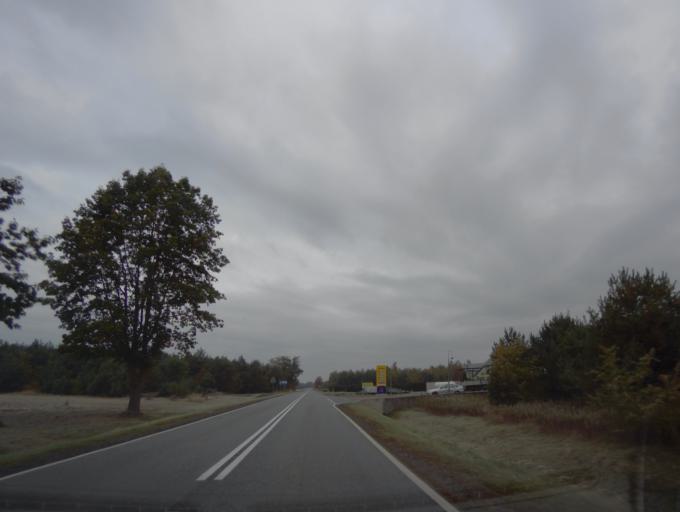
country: PL
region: Subcarpathian Voivodeship
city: Nowa Sarzyna
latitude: 50.3493
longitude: 22.3238
